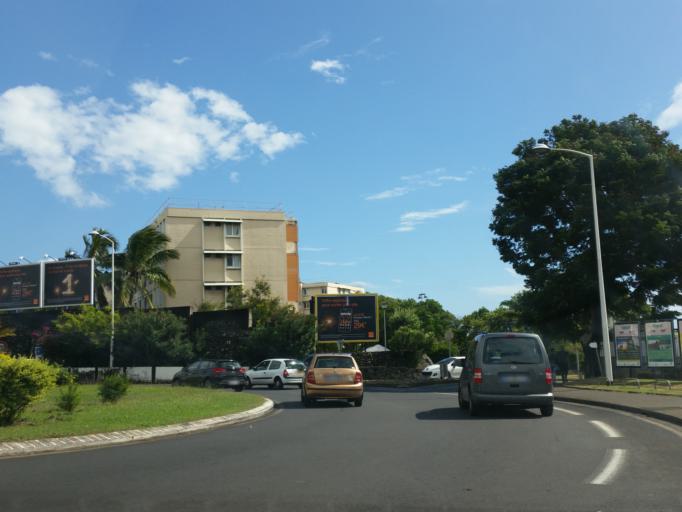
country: RE
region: Reunion
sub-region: Reunion
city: Saint-Denis
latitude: -20.9008
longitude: 55.4924
